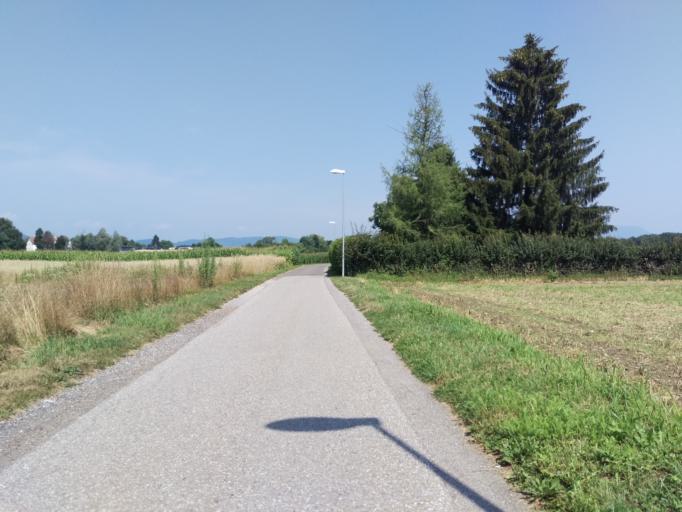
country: AT
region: Styria
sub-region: Politischer Bezirk Graz-Umgebung
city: Feldkirchen bei Graz
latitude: 47.0012
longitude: 15.4557
